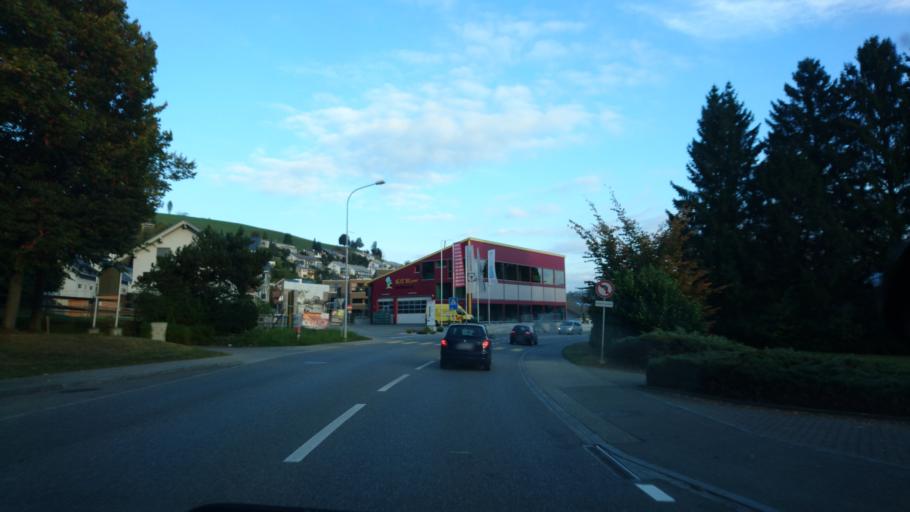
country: CH
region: Bern
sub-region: Bern-Mittelland District
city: Biglen
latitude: 46.9094
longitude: 7.6350
